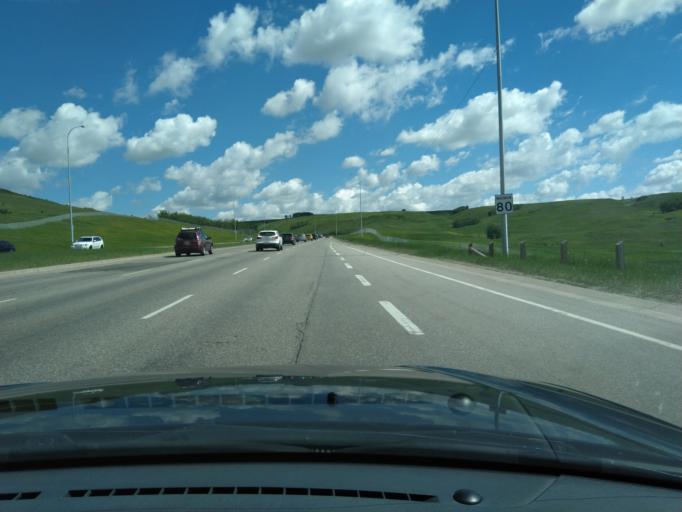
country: CA
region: Alberta
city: Calgary
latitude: 51.1112
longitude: -114.1381
